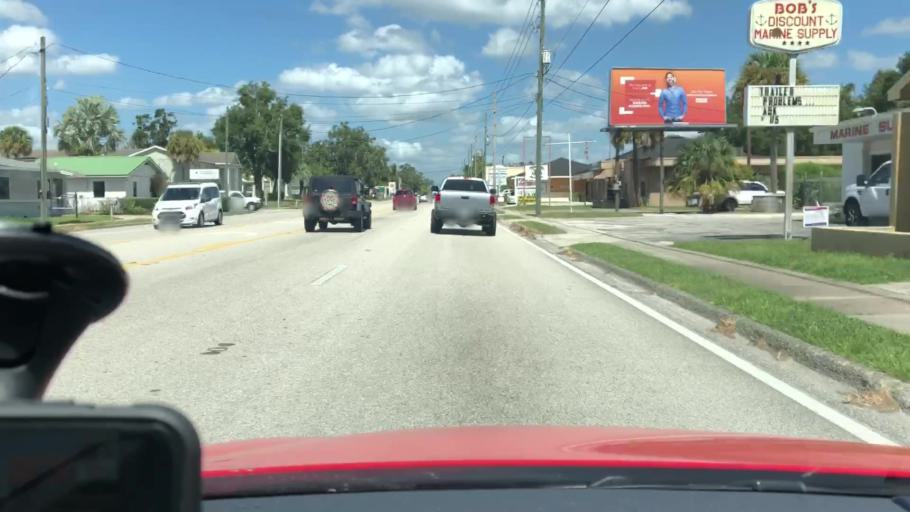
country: US
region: Florida
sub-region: Volusia County
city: West DeLand
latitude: 29.0245
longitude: -81.3240
